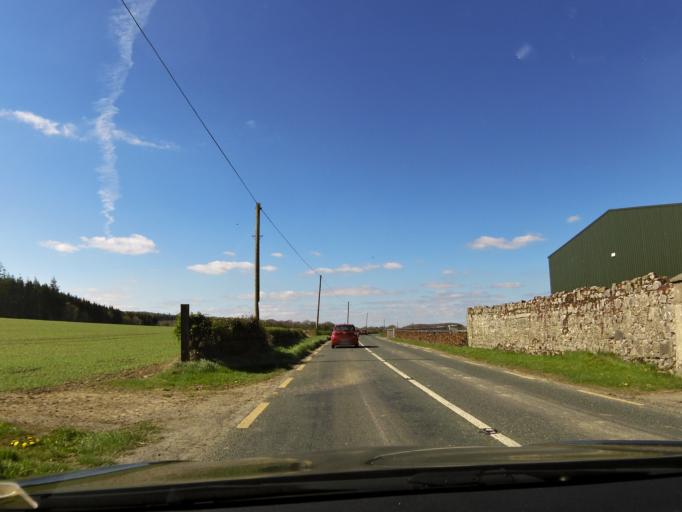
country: IE
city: Ballylinan
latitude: 53.0067
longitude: -7.0787
